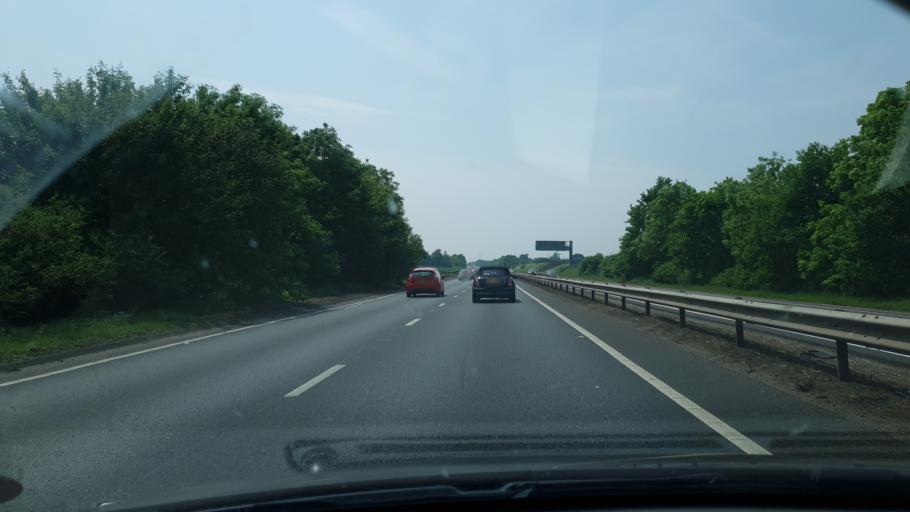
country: GB
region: England
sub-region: Suffolk
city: Capel Saint Mary
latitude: 52.0227
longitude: 1.0842
